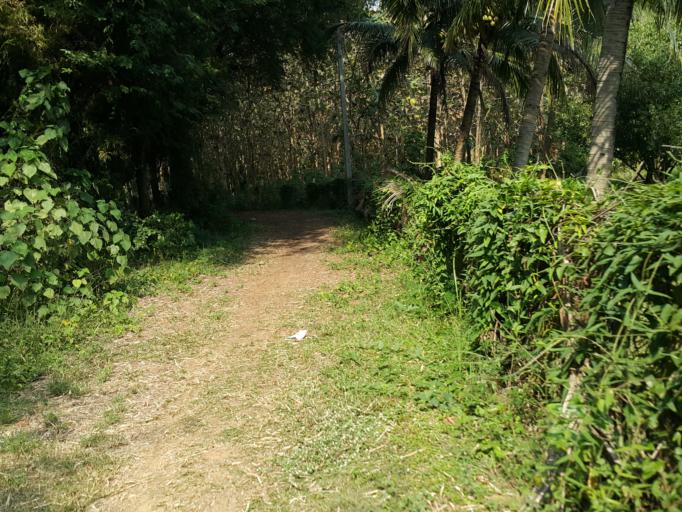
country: TH
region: Sukhothai
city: Thung Saliam
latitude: 17.3228
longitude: 99.5270
